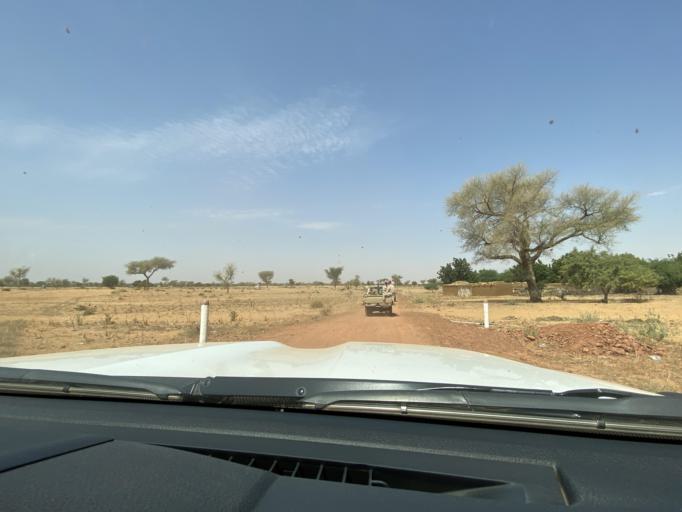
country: NE
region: Dosso
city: Birnin Gaoure
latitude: 13.2421
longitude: 2.8659
